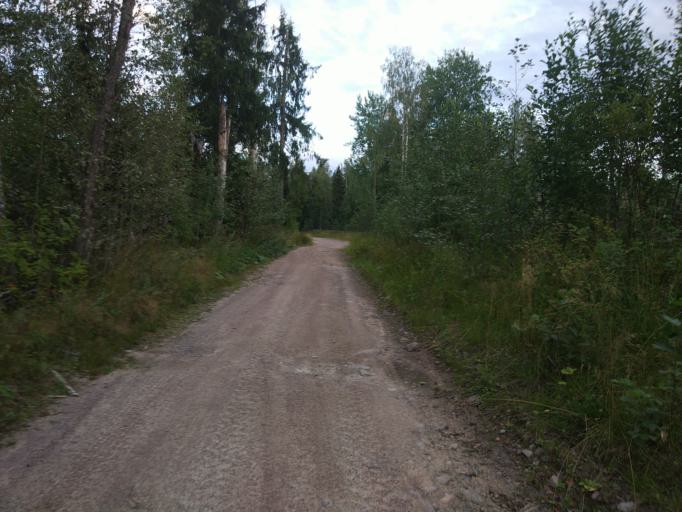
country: RU
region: Leningrad
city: Kuznechnoye
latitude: 61.1101
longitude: 29.6134
